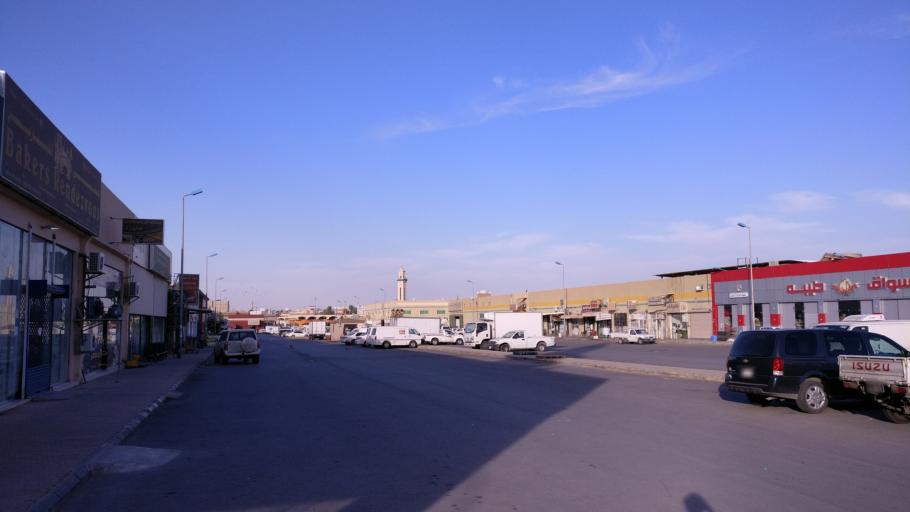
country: SA
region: Al-Qassim
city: Unaizah
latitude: 26.0874
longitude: 43.9692
